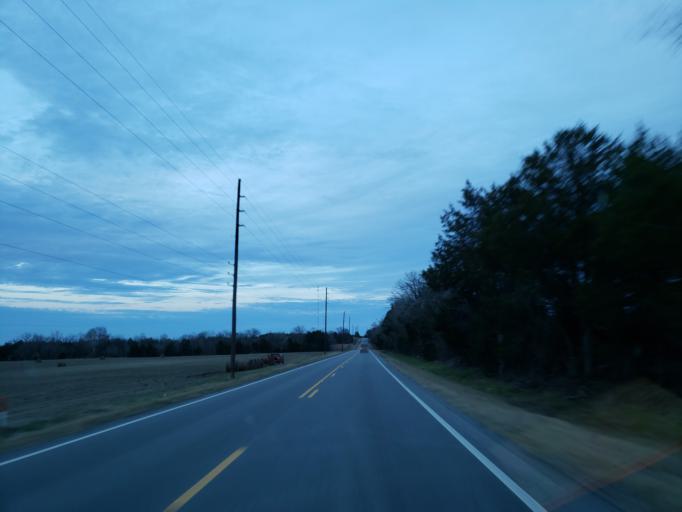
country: US
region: Alabama
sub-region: Sumter County
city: Livingston
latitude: 32.8053
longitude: -88.3053
